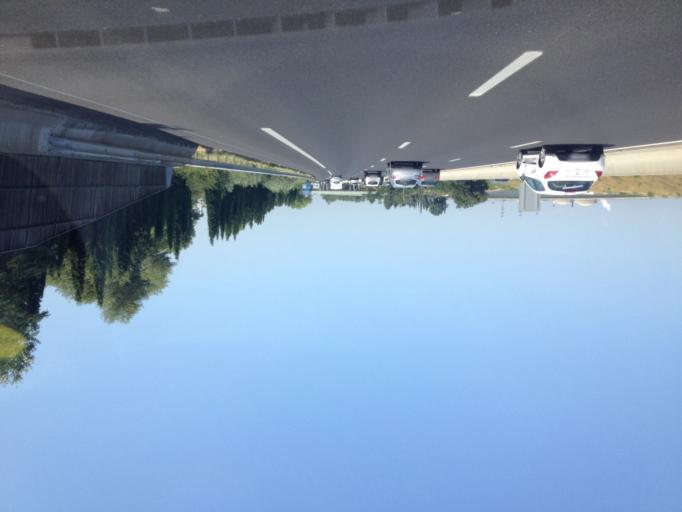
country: FR
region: Provence-Alpes-Cote d'Azur
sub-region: Departement du Vaucluse
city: Bollene
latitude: 44.3199
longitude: 4.7409
